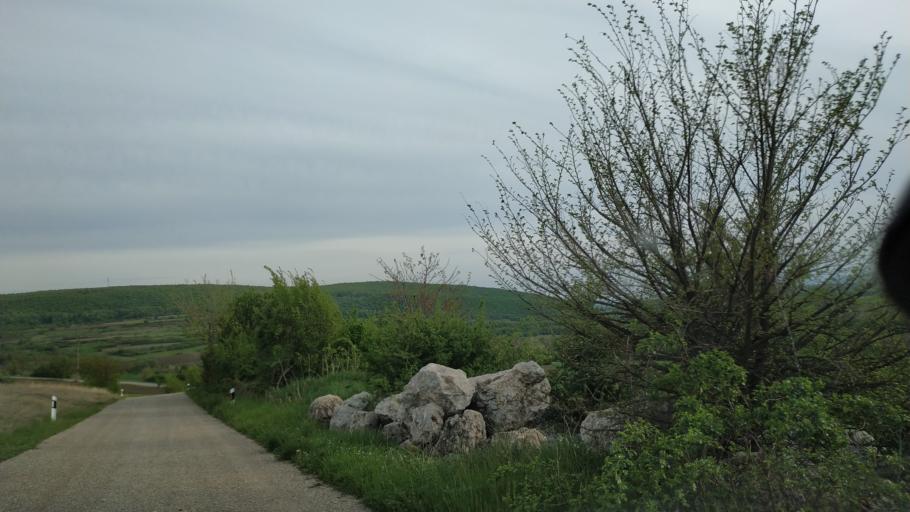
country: RS
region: Central Serbia
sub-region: Zajecarski Okrug
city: Soko Banja
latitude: 43.5230
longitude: 21.8710
